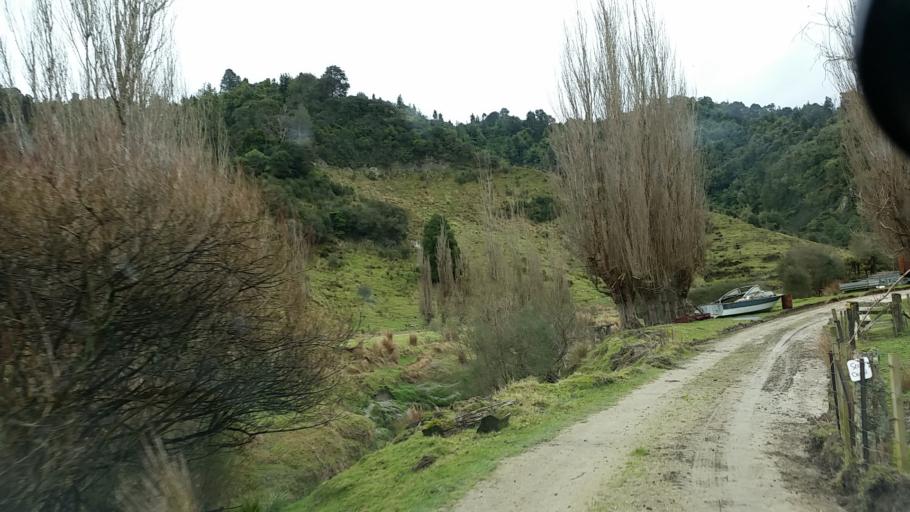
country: NZ
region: Taranaki
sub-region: South Taranaki District
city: Patea
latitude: -39.6553
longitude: 174.7518
